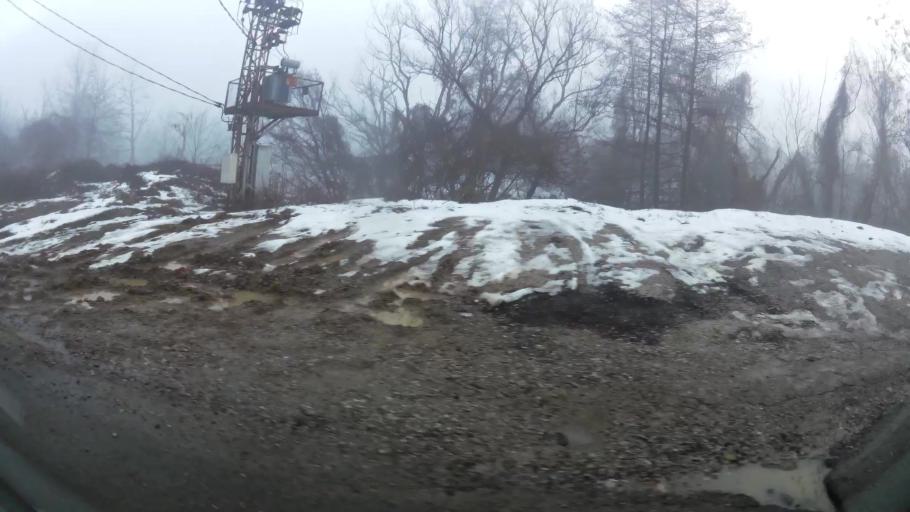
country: BG
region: Sofia-Capital
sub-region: Stolichna Obshtina
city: Sofia
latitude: 42.6578
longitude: 23.2526
